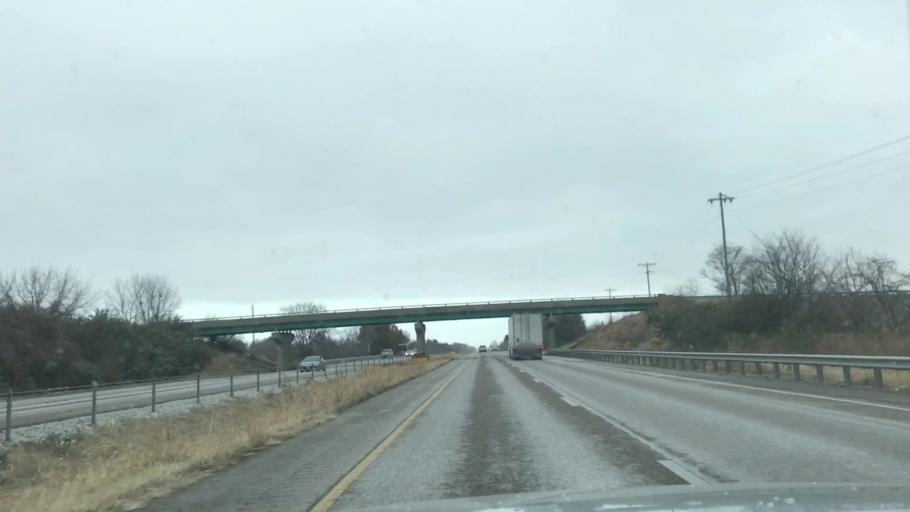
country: US
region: Illinois
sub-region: Madison County
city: Troy
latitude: 38.7583
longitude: -89.9054
